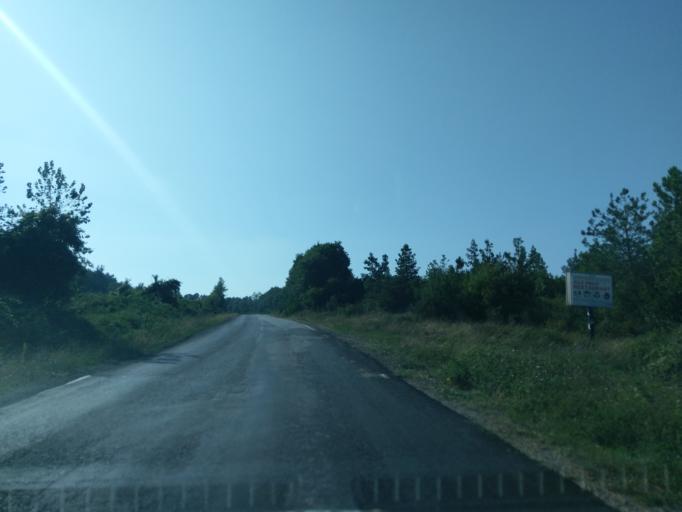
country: TR
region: Sinop
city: Erfelek
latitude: 41.9497
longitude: 34.7705
